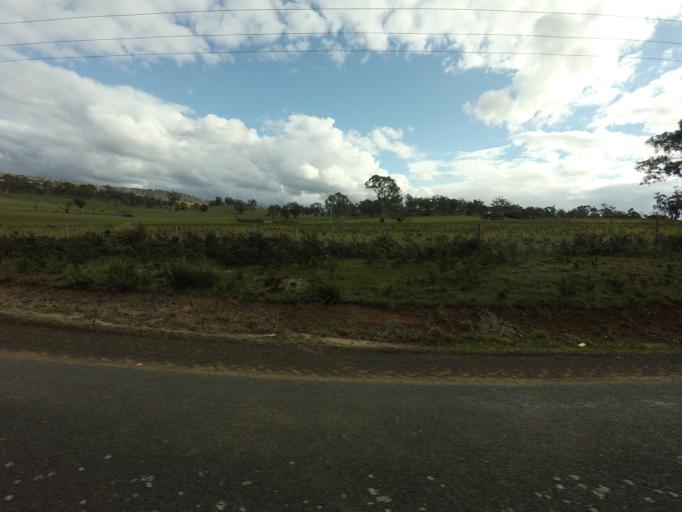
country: AU
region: Tasmania
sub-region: Northern Midlands
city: Evandale
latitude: -41.8758
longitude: 147.3038
